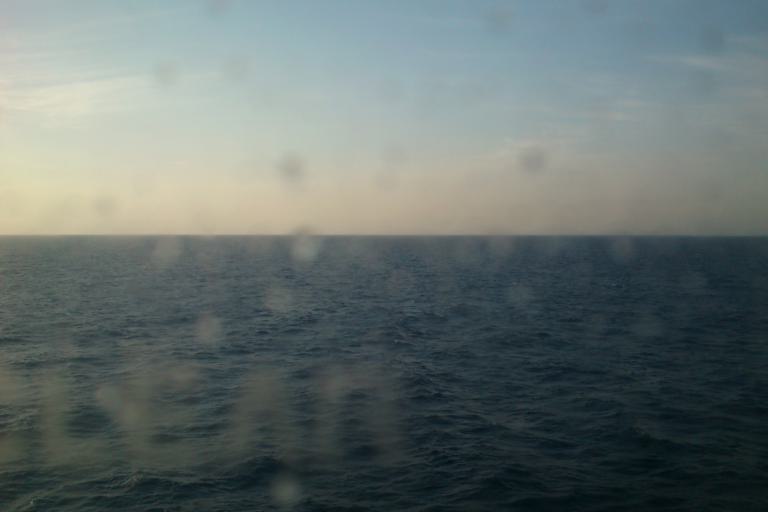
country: JP
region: Ishikawa
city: Nanao
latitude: 37.7058
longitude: 136.3796
